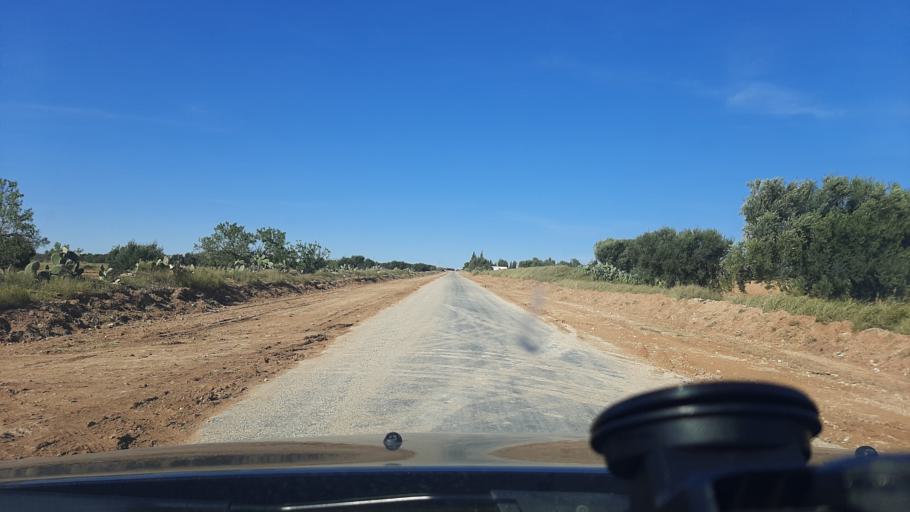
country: TN
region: Safaqis
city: Sfax
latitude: 34.9387
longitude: 10.5599
